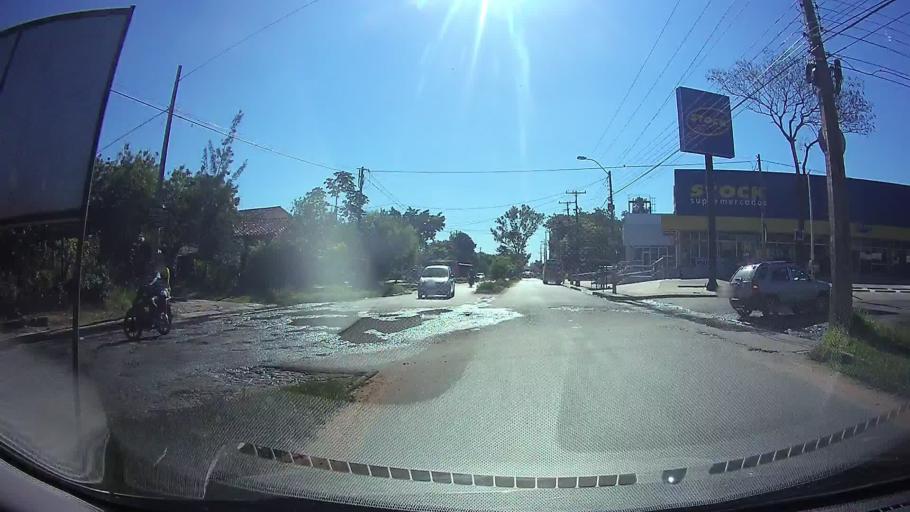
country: PY
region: Central
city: Fernando de la Mora
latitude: -25.2964
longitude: -57.5225
